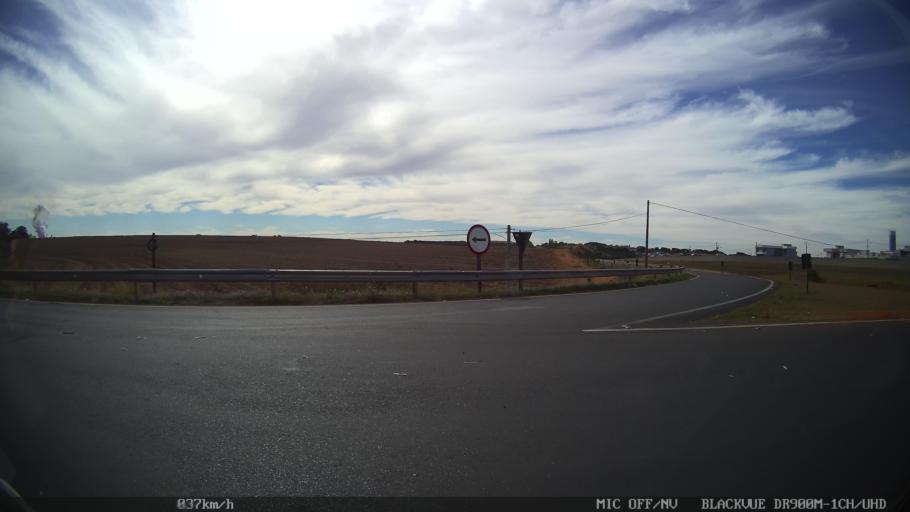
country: BR
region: Sao Paulo
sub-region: Catanduva
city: Catanduva
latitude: -21.1148
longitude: -48.9784
